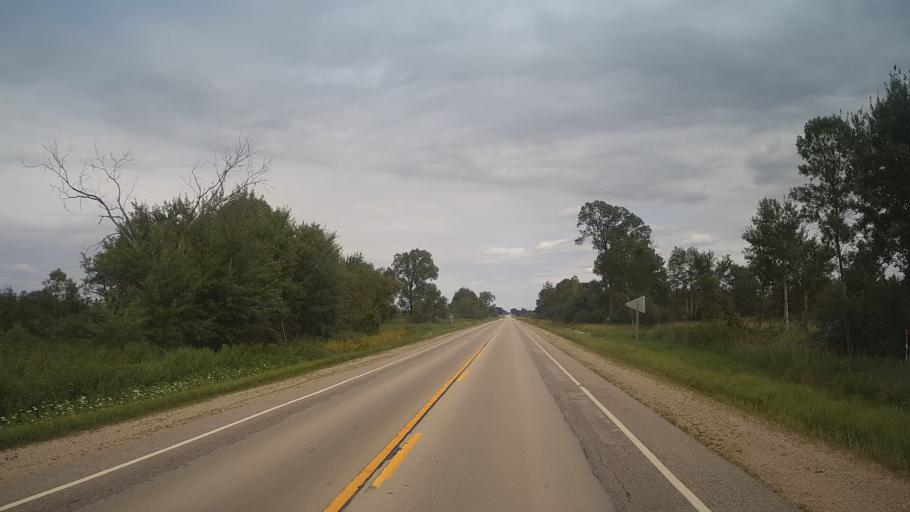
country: US
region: Wisconsin
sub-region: Green Lake County
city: Berlin
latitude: 44.0487
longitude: -88.9675
